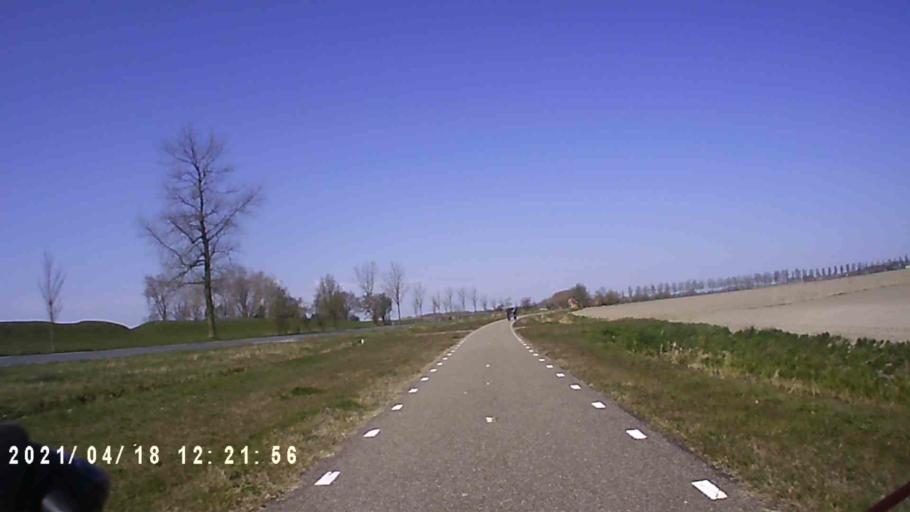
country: NL
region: Friesland
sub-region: Gemeente Kollumerland en Nieuwkruisland
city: Kollum
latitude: 53.3222
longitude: 6.1305
